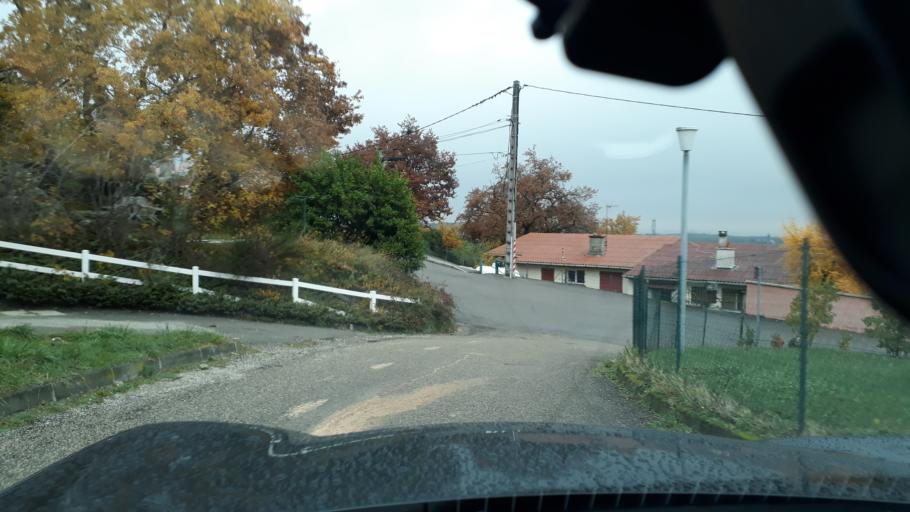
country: FR
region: Rhone-Alpes
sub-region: Departement de l'Ardeche
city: Felines
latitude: 45.3101
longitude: 4.7249
